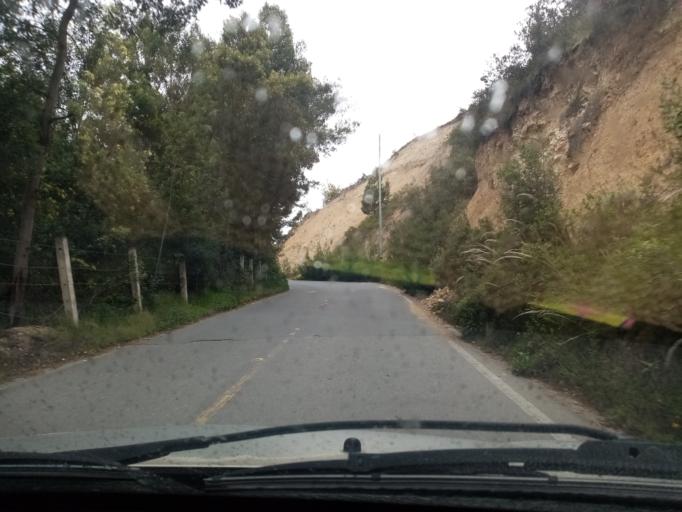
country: CO
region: Boyaca
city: Siachoque
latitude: 5.5693
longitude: -73.2527
